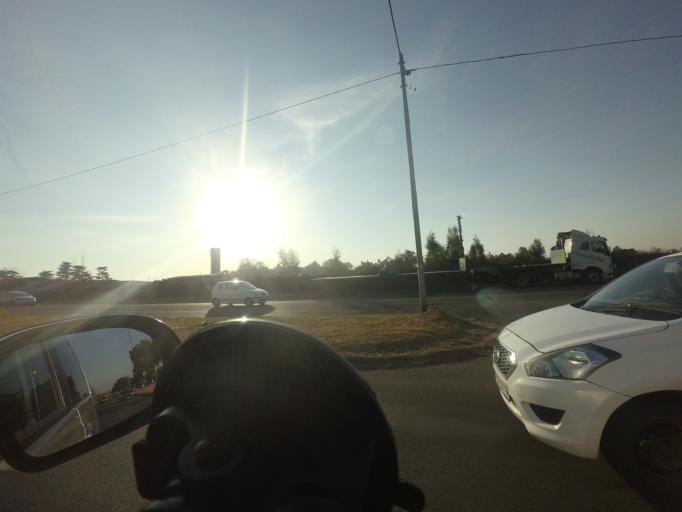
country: ZA
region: Gauteng
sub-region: Sedibeng District Municipality
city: Vereeniging
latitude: -26.6601
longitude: 27.9503
